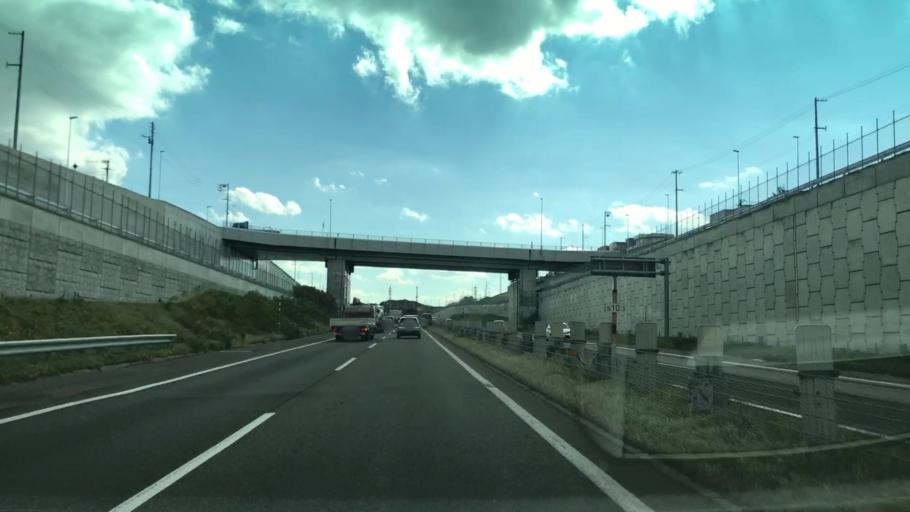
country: JP
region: Hokkaido
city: Kitahiroshima
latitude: 42.9939
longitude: 141.4691
